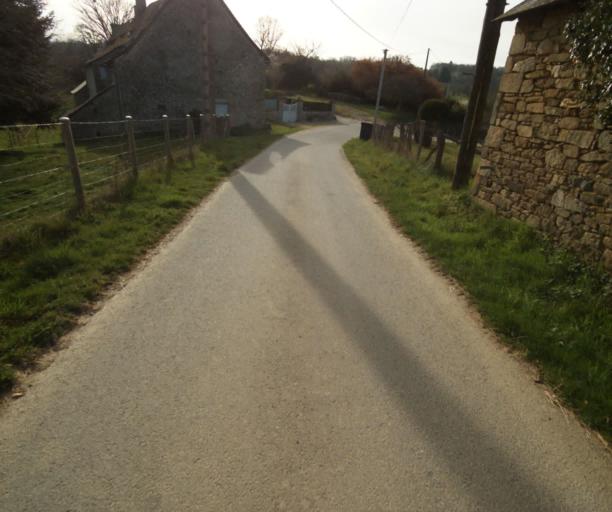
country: FR
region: Limousin
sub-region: Departement de la Correze
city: Chamboulive
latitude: 45.4461
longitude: 1.7529
